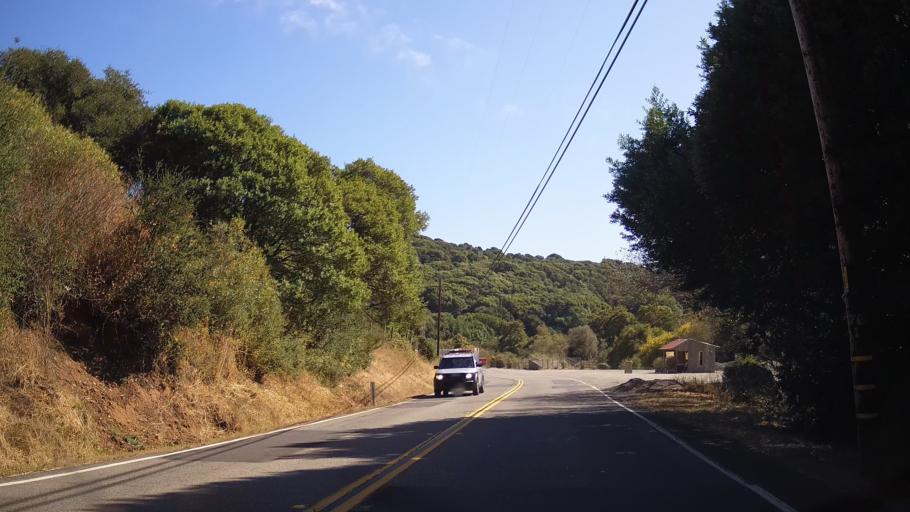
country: US
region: California
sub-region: Marin County
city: Inverness
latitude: 38.0726
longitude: -122.7705
